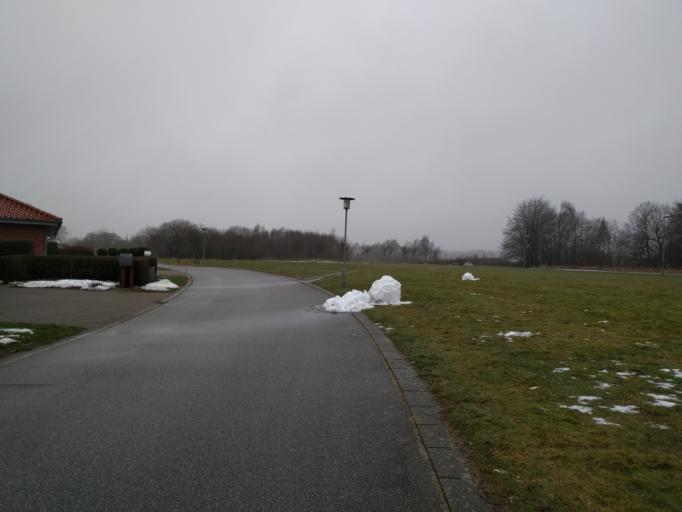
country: DK
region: Central Jutland
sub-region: Viborg Kommune
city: Viborg
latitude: 56.4309
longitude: 9.4082
